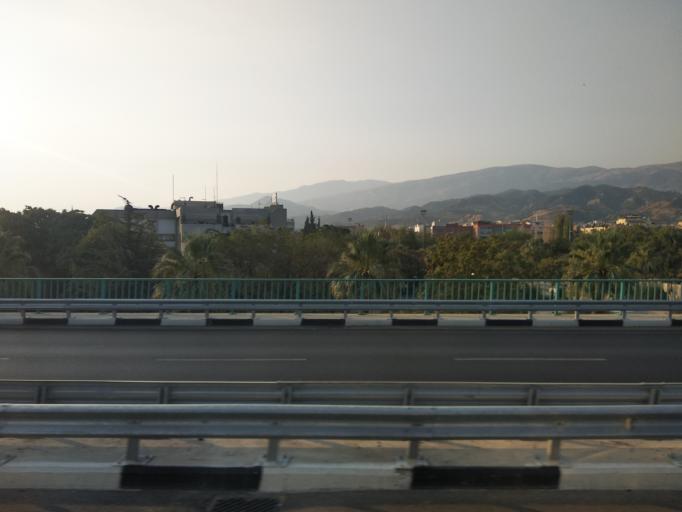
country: TR
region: Manisa
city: Salihli
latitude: 38.4894
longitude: 28.1363
